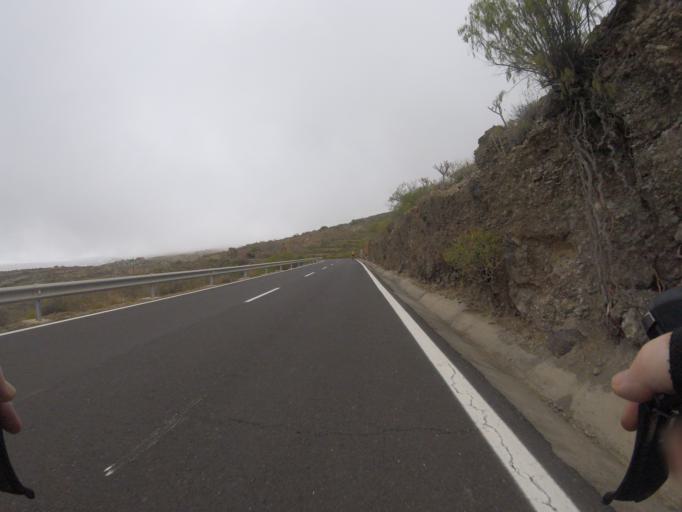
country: ES
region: Canary Islands
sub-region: Provincia de Santa Cruz de Tenerife
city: Lomo de Arico
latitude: 28.1999
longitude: -16.4646
